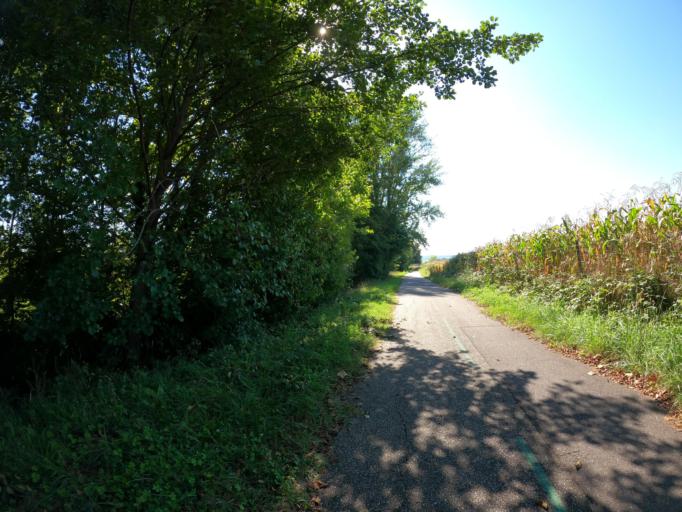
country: FR
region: Aquitaine
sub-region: Departement du Lot-et-Garonne
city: Bias
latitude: 44.4139
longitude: 0.6625
